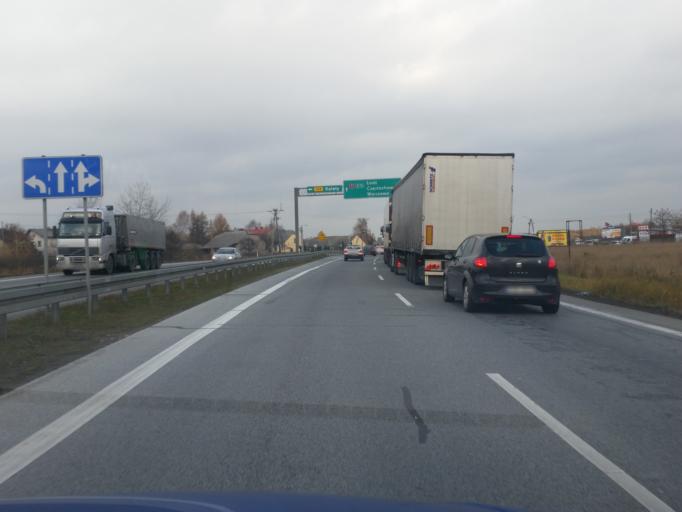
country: PL
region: Silesian Voivodeship
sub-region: Powiat myszkowski
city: Kozieglowy
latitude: 50.5964
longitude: 19.1499
